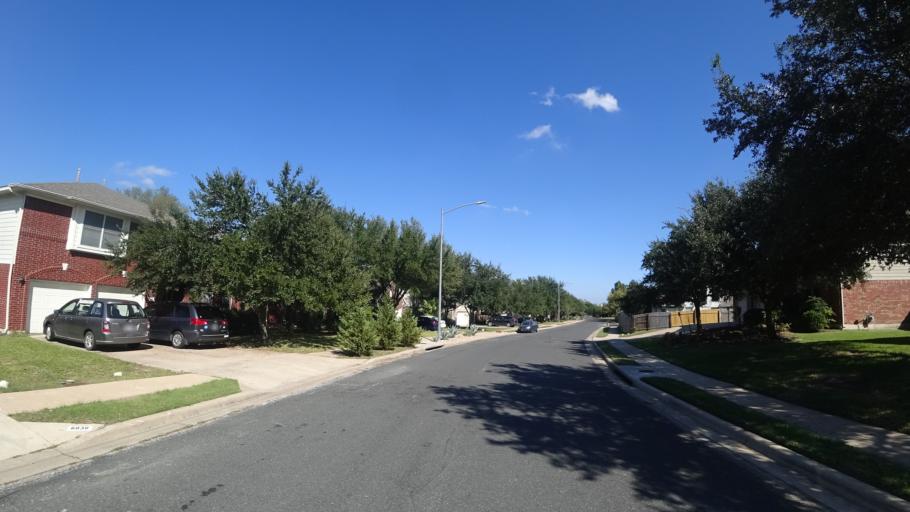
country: US
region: Texas
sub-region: Travis County
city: Manor
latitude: 30.3500
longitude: -97.6119
